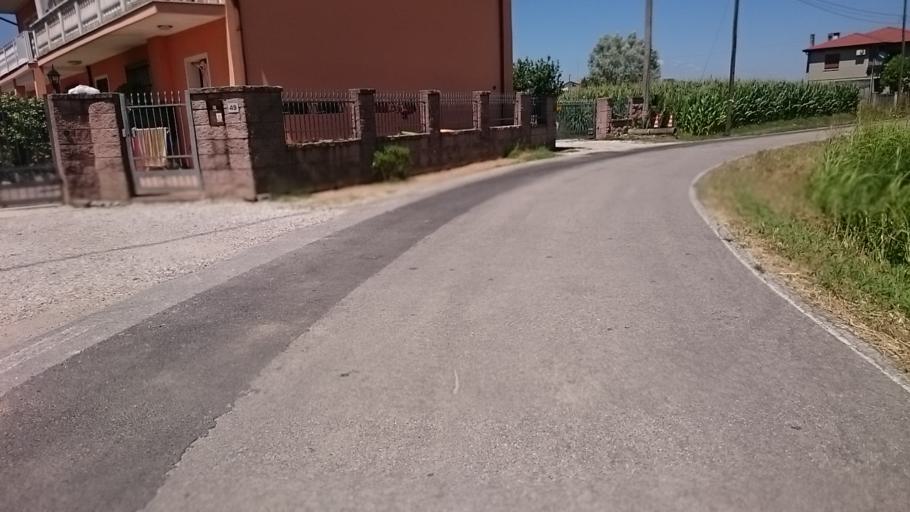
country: IT
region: Veneto
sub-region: Provincia di Padova
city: Campodarsego
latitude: 45.5036
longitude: 11.9361
